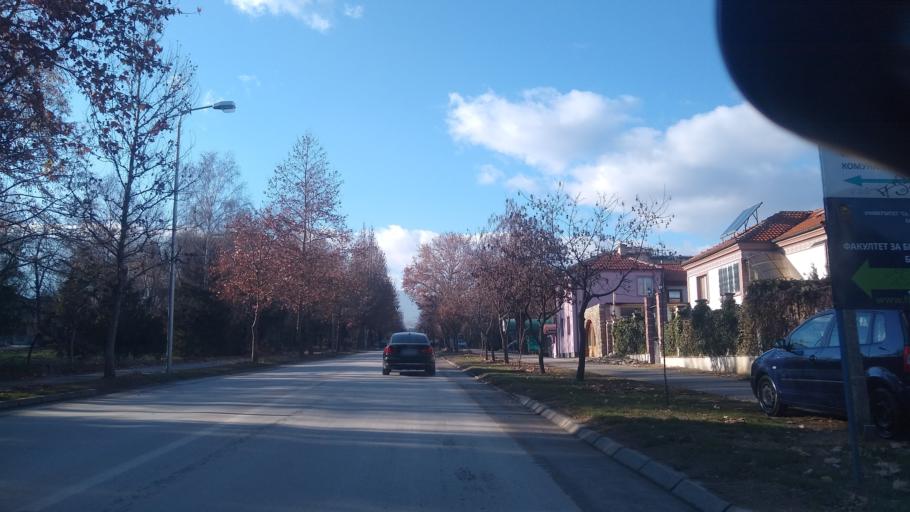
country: MK
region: Bitola
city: Bitola
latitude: 41.0235
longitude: 21.3269
